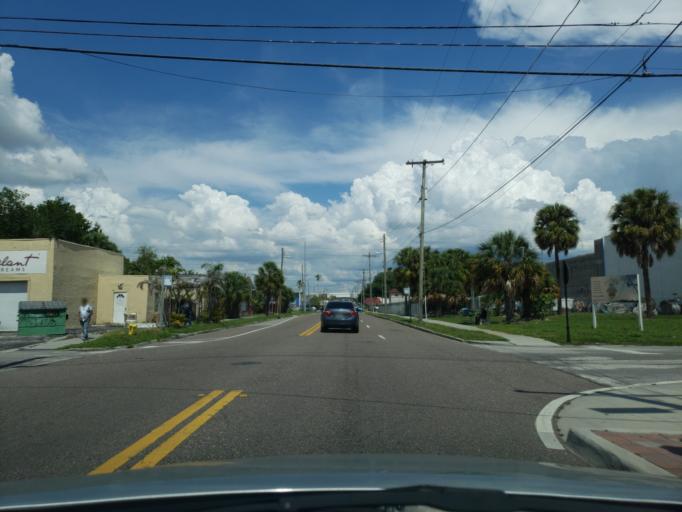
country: US
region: Florida
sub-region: Hillsborough County
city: Tampa
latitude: 27.9602
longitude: -82.4324
